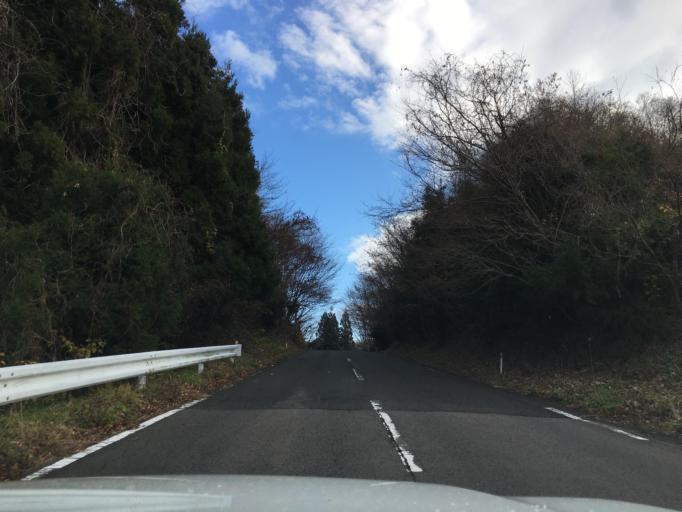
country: JP
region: Fukushima
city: Fukushima-shi
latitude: 37.6381
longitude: 140.5895
